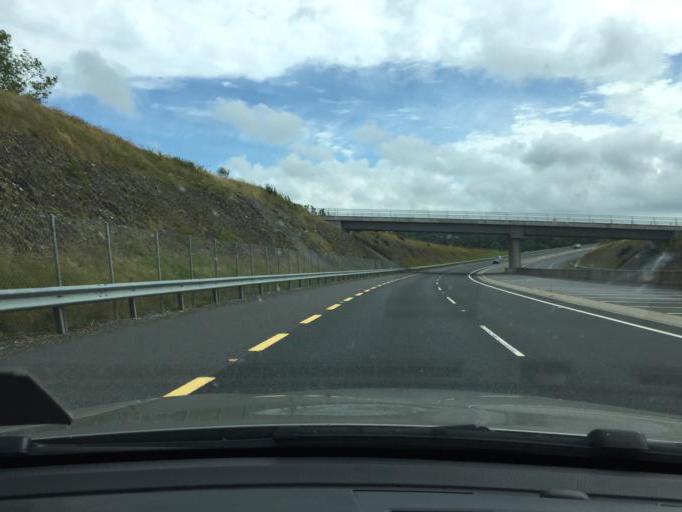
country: IE
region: Leinster
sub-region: Kilkenny
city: Mooncoin
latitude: 52.2443
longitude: -7.1891
